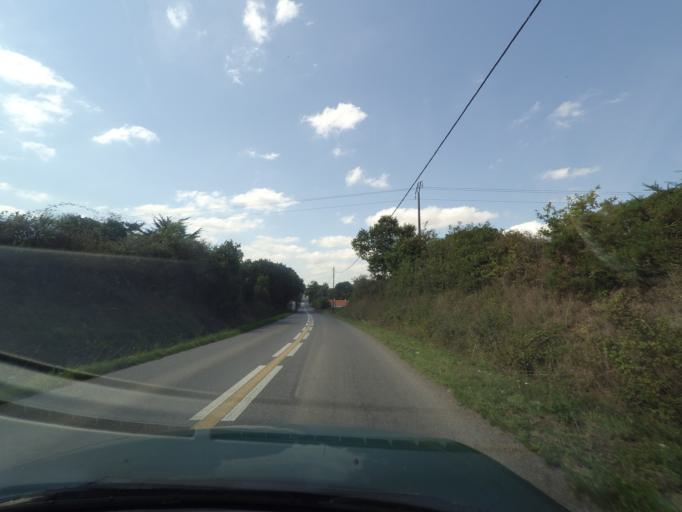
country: FR
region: Pays de la Loire
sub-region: Departement de la Loire-Atlantique
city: Sainte-Pazanne
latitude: 47.0776
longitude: -1.7877
